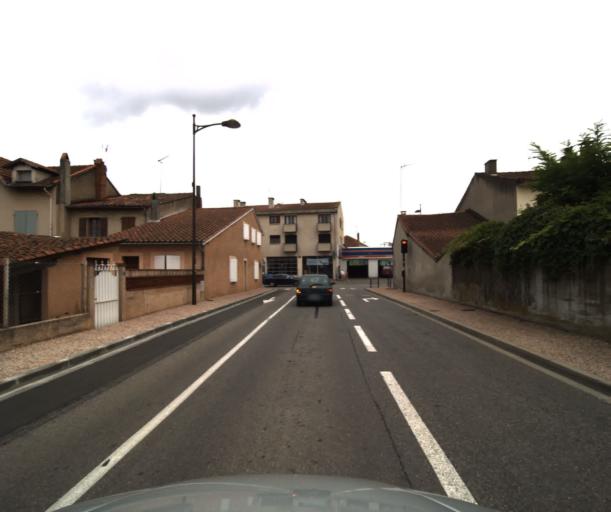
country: FR
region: Midi-Pyrenees
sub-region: Departement de la Haute-Garonne
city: Muret
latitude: 43.4649
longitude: 1.3259
